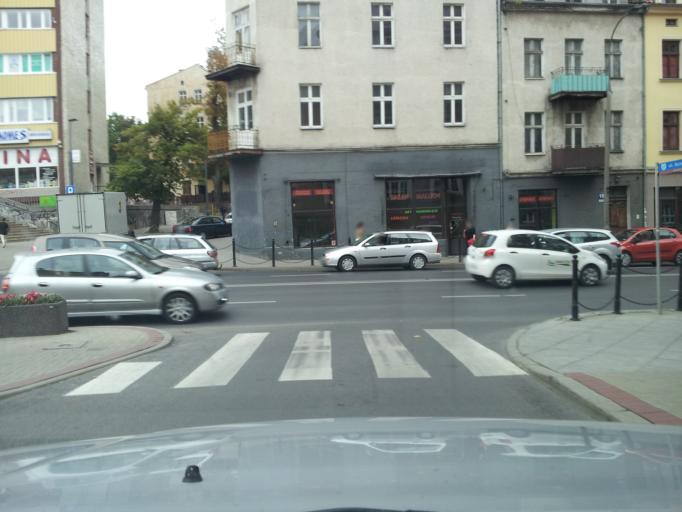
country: PL
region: Warmian-Masurian Voivodeship
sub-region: Powiat olsztynski
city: Olsztyn
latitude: 53.7794
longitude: 20.4800
